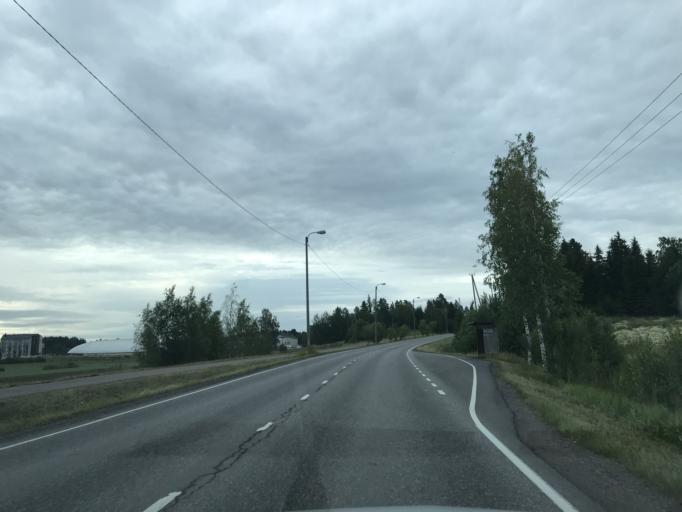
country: FI
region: Uusimaa
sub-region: Helsinki
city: Nurmijaervi
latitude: 60.3837
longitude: 24.7277
